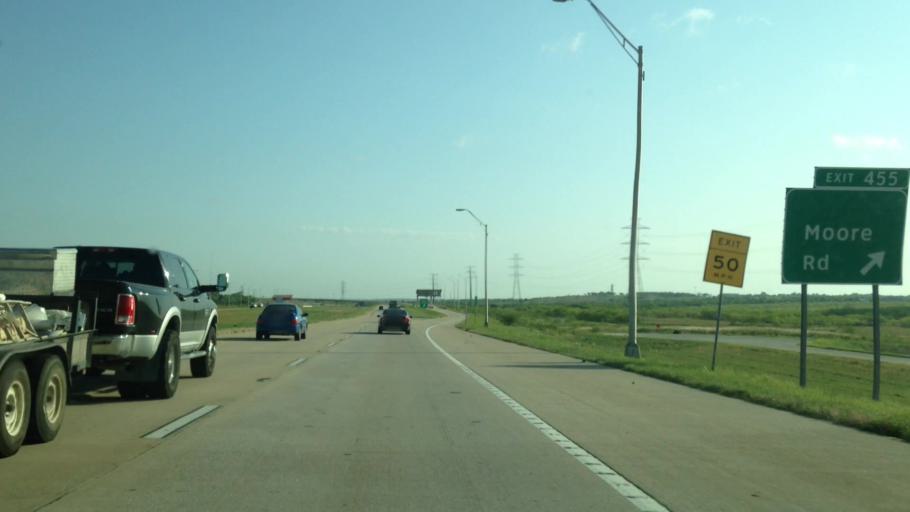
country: US
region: Texas
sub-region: Travis County
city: Onion Creek
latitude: 30.1064
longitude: -97.6655
